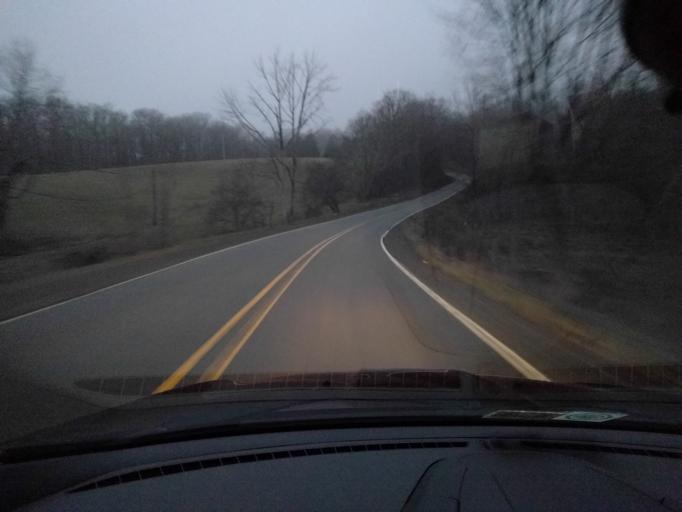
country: US
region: West Virginia
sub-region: Greenbrier County
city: Rainelle
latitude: 37.9697
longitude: -80.8089
